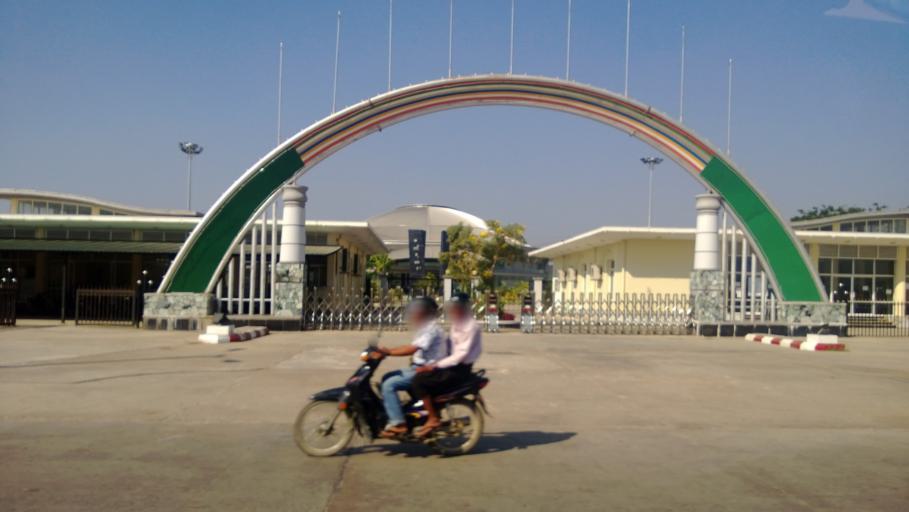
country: MM
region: Mandalay
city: Nay Pyi Taw
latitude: 19.7438
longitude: 96.1142
